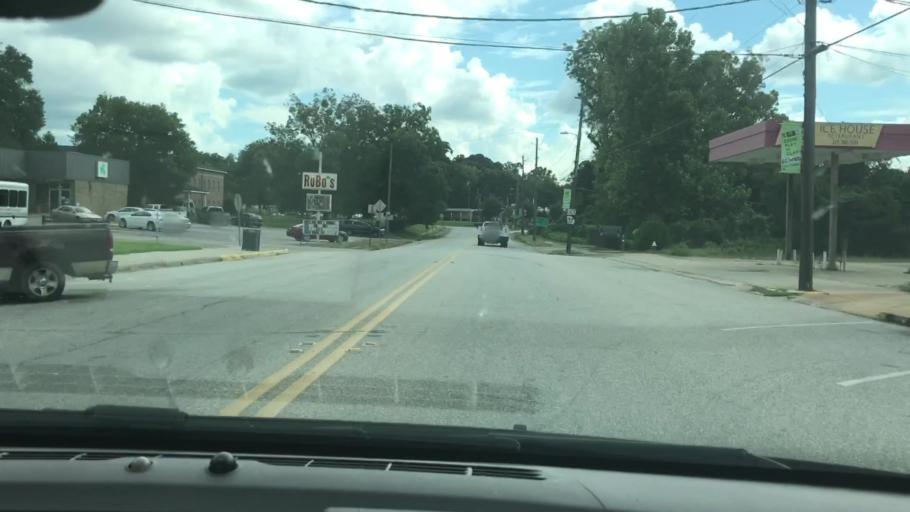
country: US
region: Georgia
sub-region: Clay County
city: Fort Gaines
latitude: 31.6054
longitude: -85.0499
